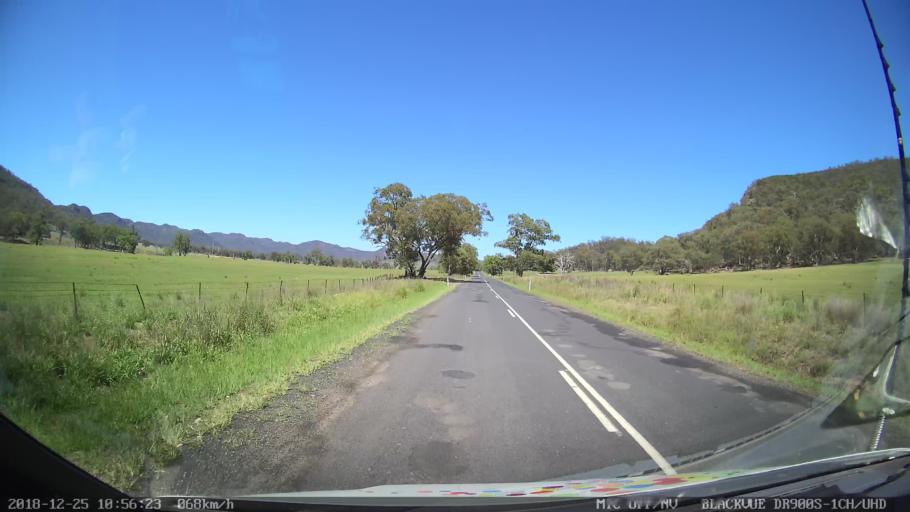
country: AU
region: New South Wales
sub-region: Upper Hunter Shire
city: Merriwa
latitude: -32.4010
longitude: 150.2633
